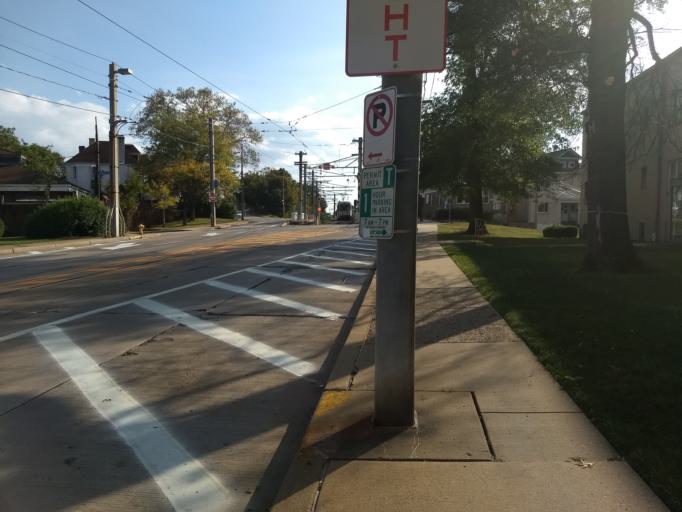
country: US
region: Pennsylvania
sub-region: Allegheny County
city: Dormont
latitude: 40.4030
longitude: -80.0308
